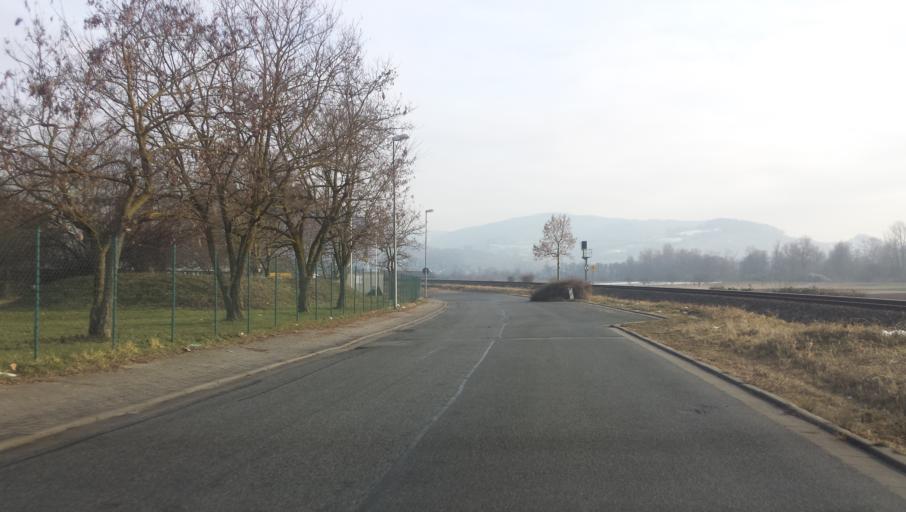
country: DE
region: Hesse
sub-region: Regierungsbezirk Darmstadt
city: Bensheim
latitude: 49.6659
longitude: 8.6124
